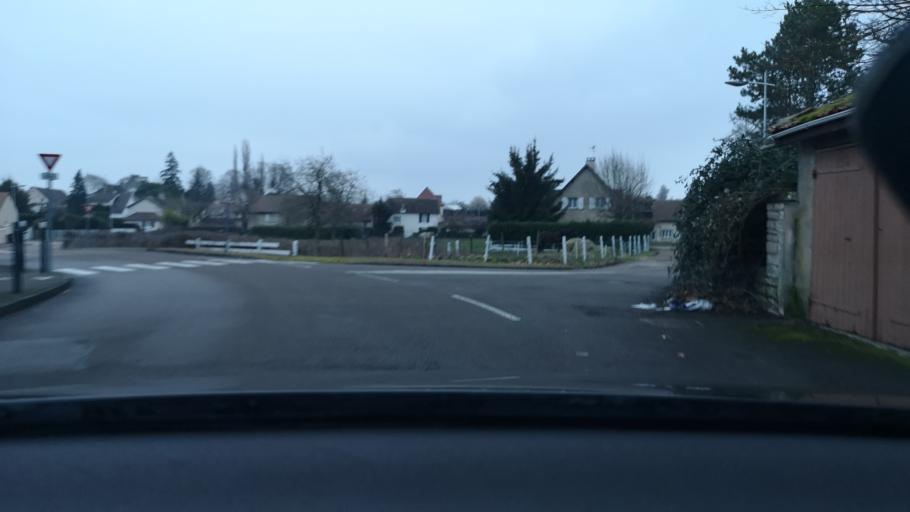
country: FR
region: Bourgogne
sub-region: Departement de Saone-et-Loire
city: Chatenoy-le-Royal
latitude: 46.7963
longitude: 4.8216
